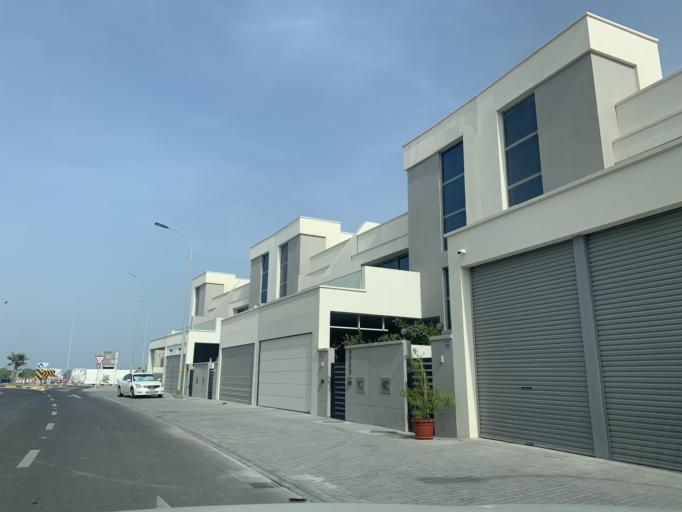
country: BH
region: Muharraq
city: Al Muharraq
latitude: 26.3131
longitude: 50.6363
